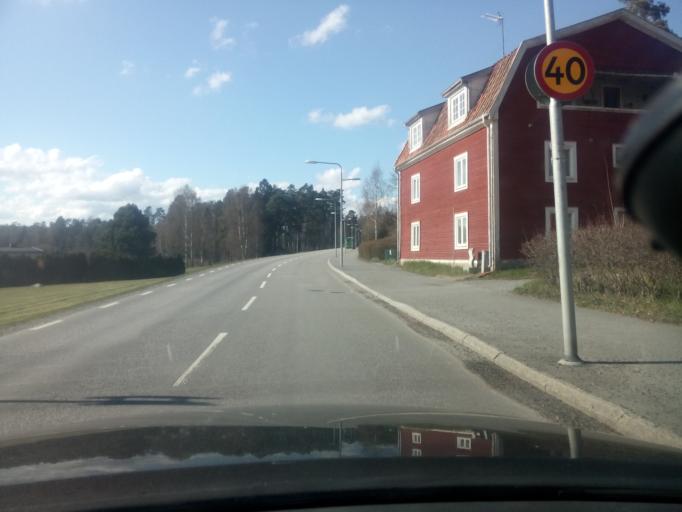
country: SE
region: Soedermanland
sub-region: Flens Kommun
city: Malmkoping
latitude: 59.1379
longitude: 16.7208
